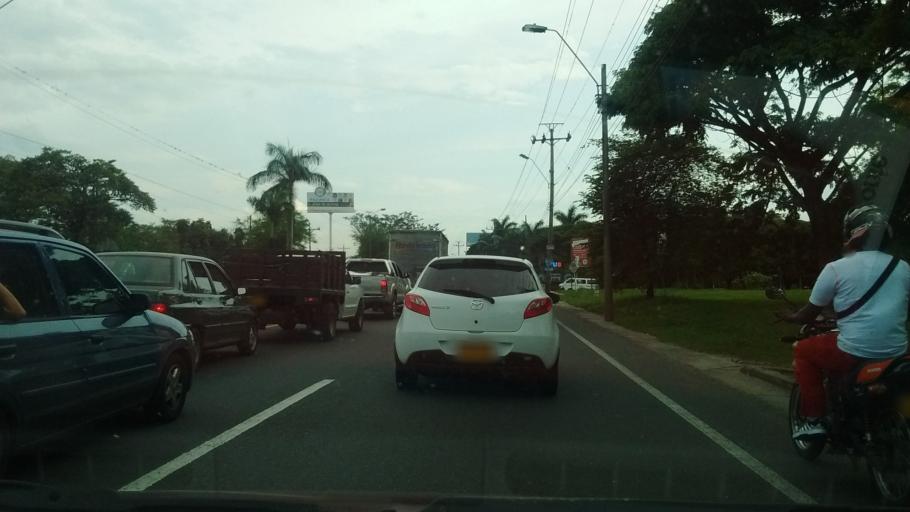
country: CO
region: Valle del Cauca
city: Jamundi
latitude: 3.3481
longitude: -76.5241
